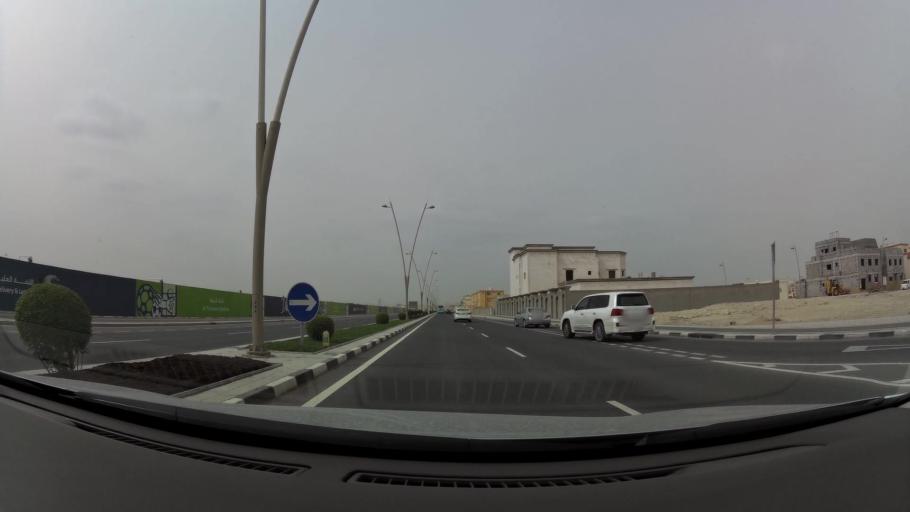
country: QA
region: Baladiyat ad Dawhah
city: Doha
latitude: 25.2333
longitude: 51.5347
